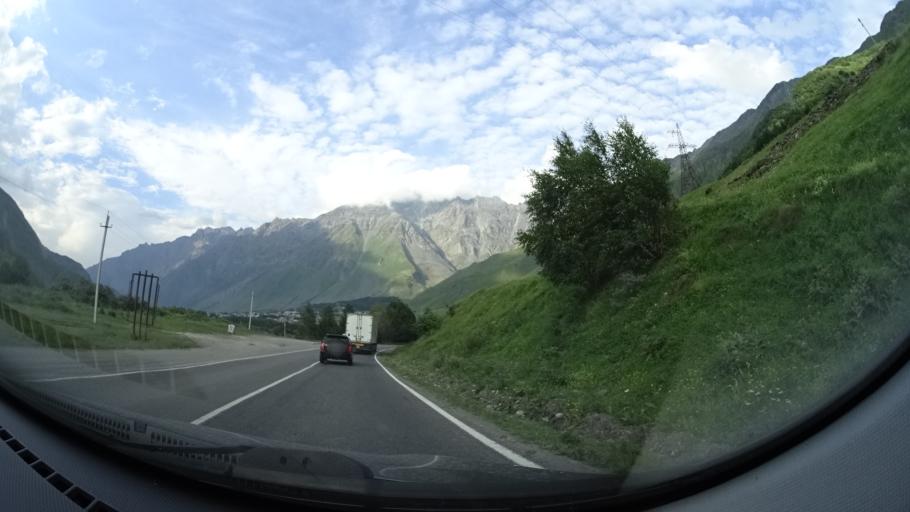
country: GE
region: Mtskheta-Mtianeti
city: Step'antsminda
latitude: 42.6415
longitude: 44.6355
